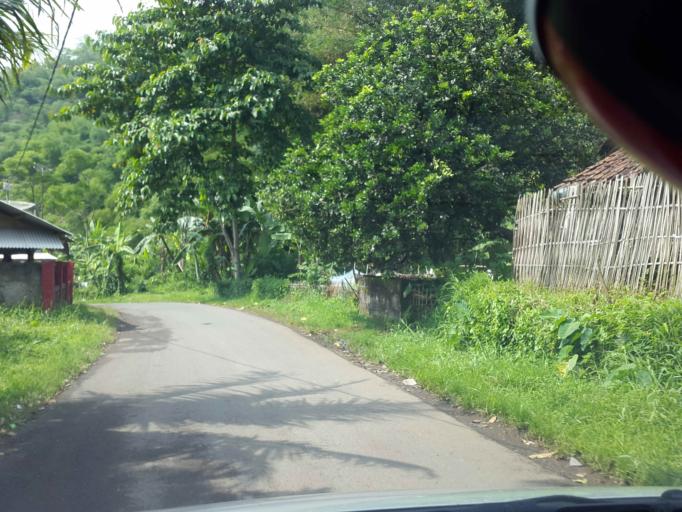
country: ID
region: West Java
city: Sukabumi
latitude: -6.9180
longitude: 107.0018
